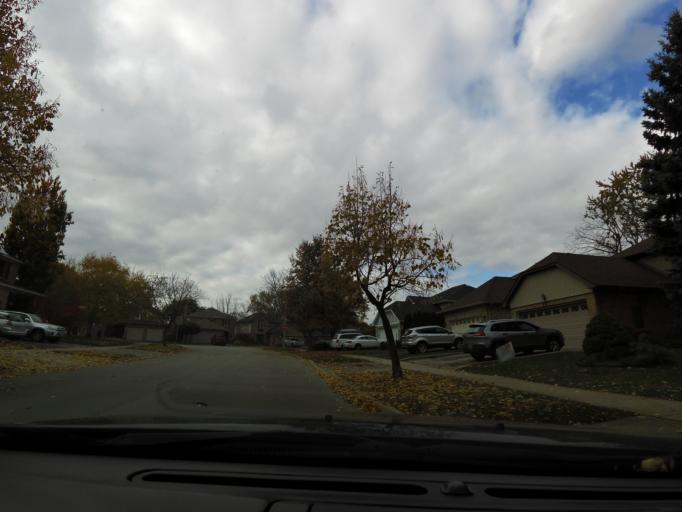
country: CA
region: Ontario
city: Burlington
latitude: 43.3279
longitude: -79.8107
